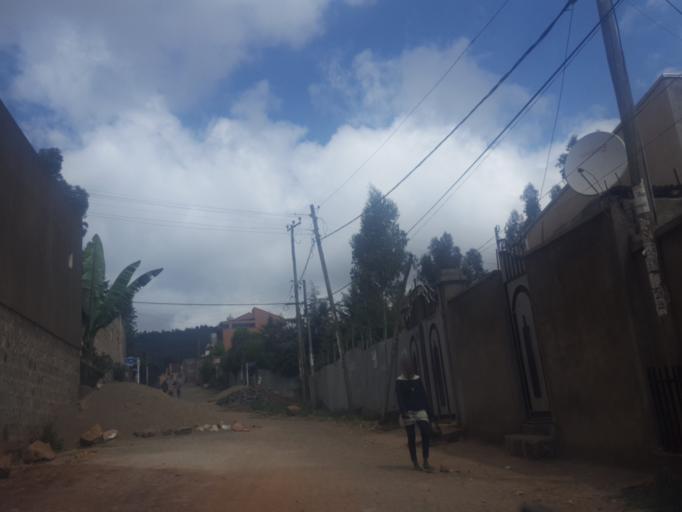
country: ET
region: Adis Abeba
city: Addis Ababa
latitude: 9.0665
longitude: 38.7367
